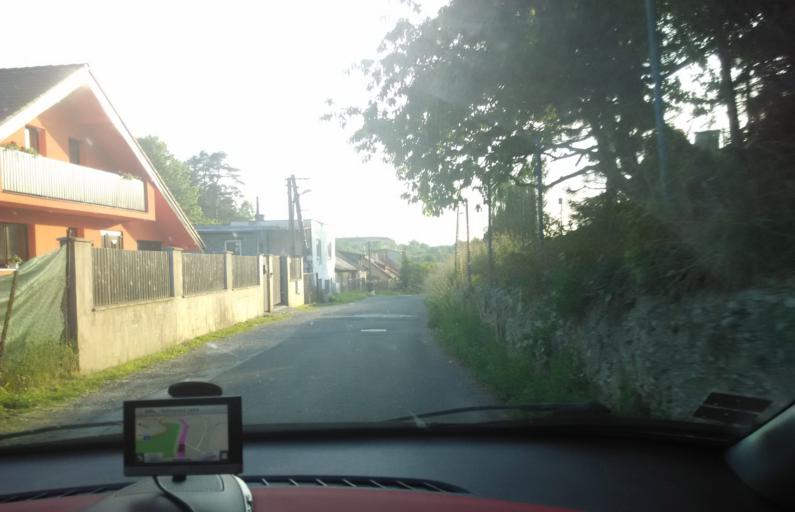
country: SK
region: Presovsky
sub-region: Okres Presov
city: Levoca
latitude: 49.0303
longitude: 20.6000
